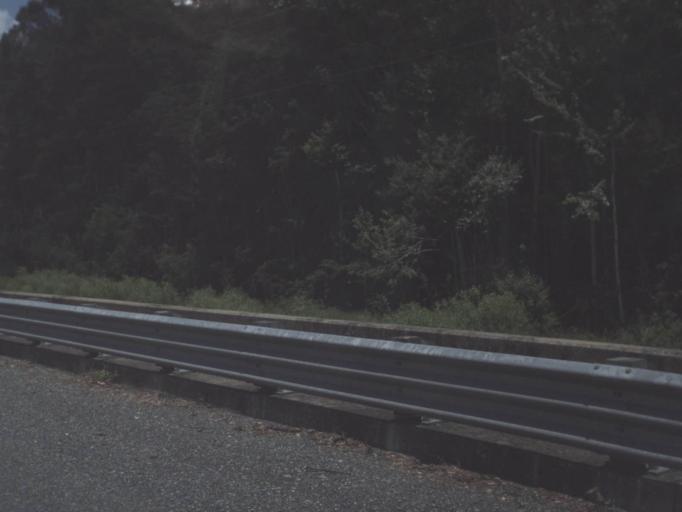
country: US
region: Florida
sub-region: Dixie County
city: Cross City
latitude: 29.6714
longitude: -83.2307
